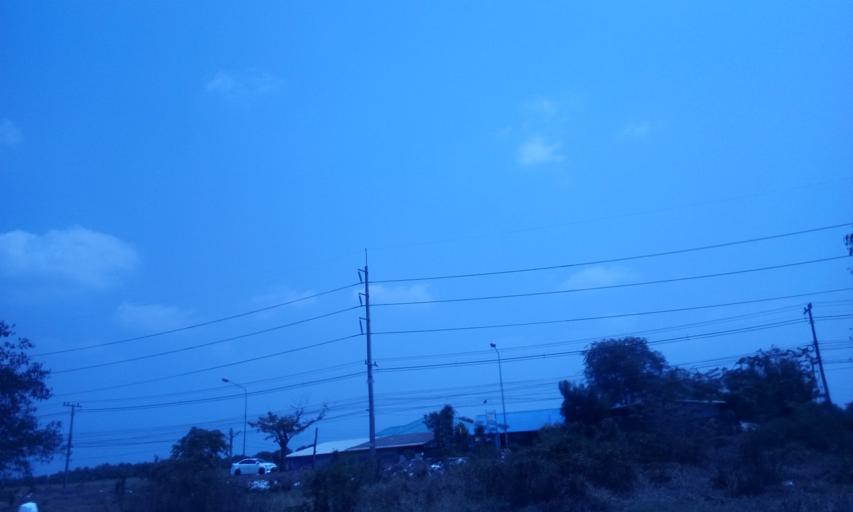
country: TH
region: Chachoengsao
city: Bang Nam Priao
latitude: 13.8305
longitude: 101.0560
